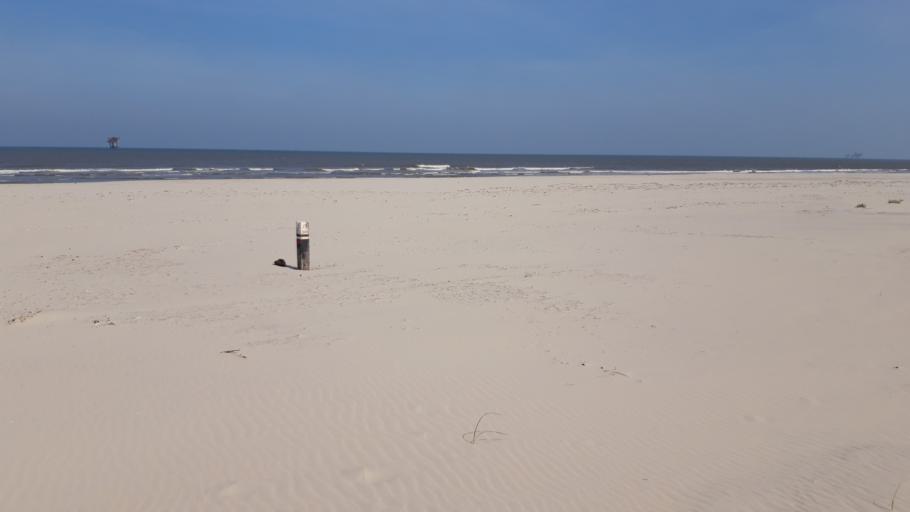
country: NL
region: Friesland
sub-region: Gemeente Ameland
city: Nes
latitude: 53.4647
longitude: 5.8640
